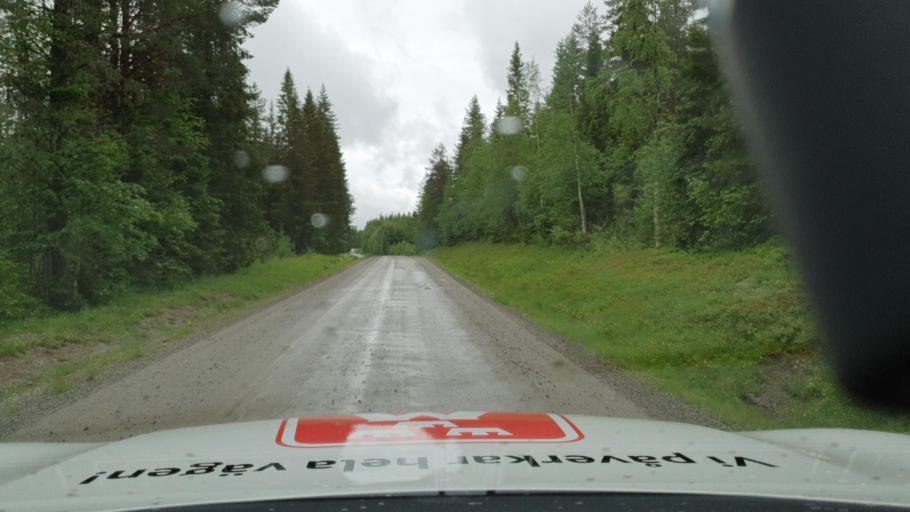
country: SE
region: Vaesterbotten
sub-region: Dorotea Kommun
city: Dorotea
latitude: 64.0512
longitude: 16.7289
